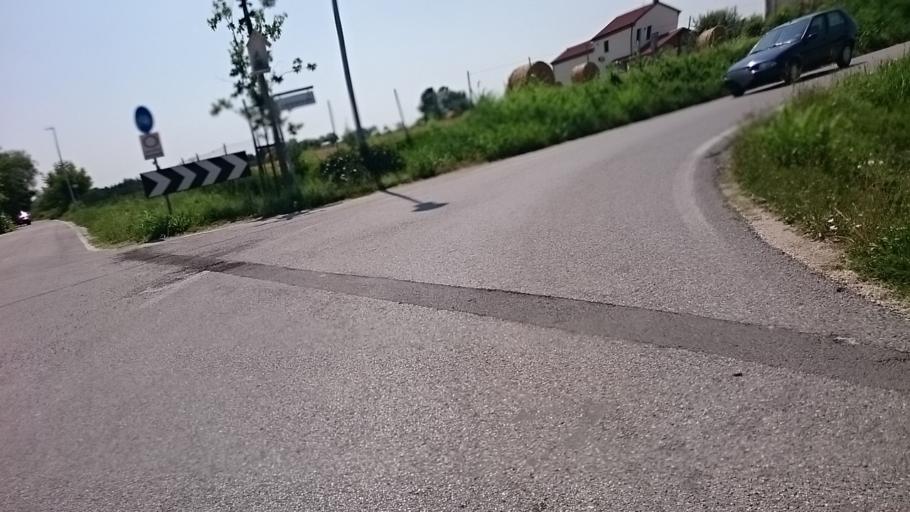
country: IT
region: Veneto
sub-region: Provincia di Padova
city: Bertipaglia
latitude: 45.3276
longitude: 11.8778
